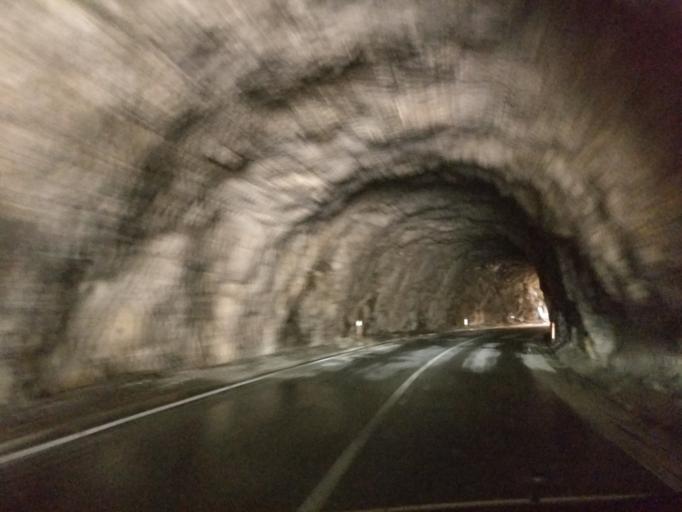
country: ME
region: Opstina Pluzine
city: Pluzine
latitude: 43.1877
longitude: 18.8523
